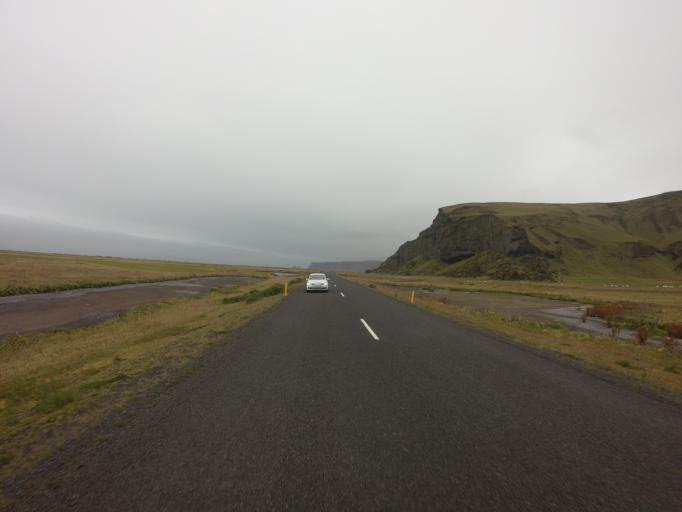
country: IS
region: South
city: Vestmannaeyjar
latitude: 63.4219
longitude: -18.9187
